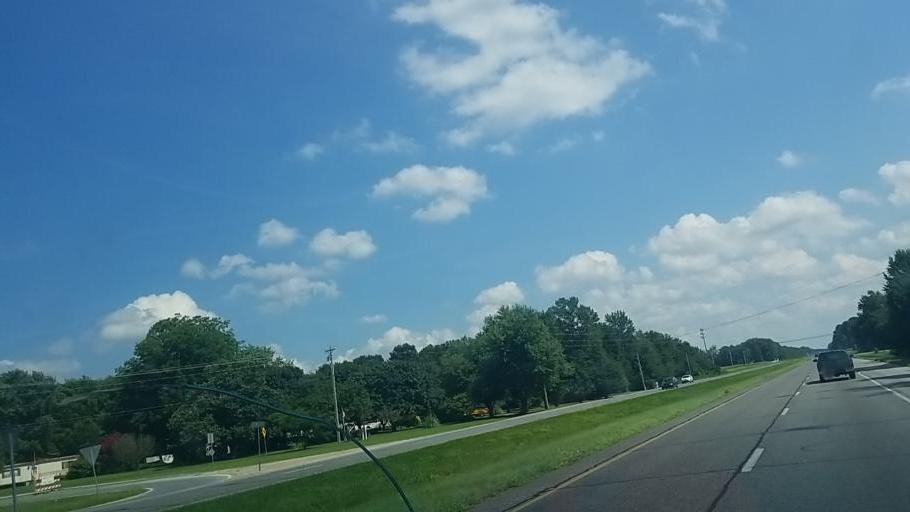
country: US
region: Delaware
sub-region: Sussex County
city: Georgetown
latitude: 38.7532
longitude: -75.4355
